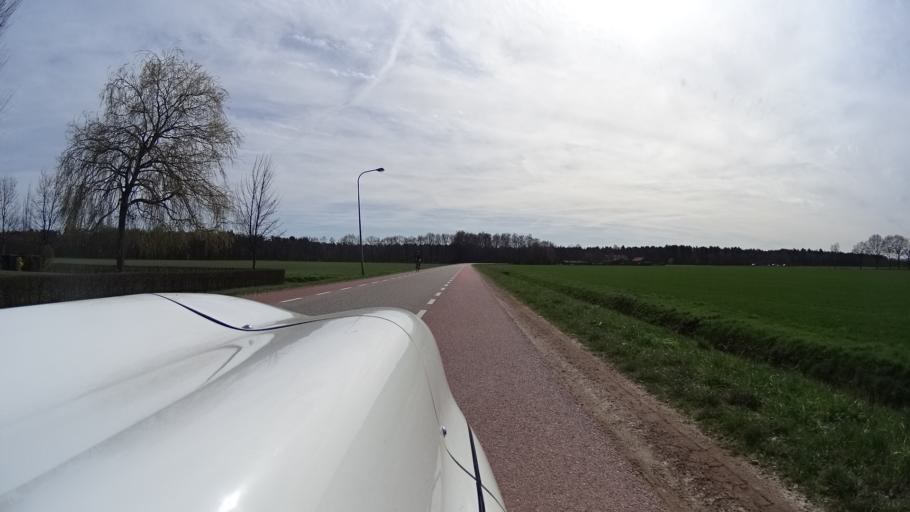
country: NL
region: Limburg
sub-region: Gemeente Venlo
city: Arcen
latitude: 51.5152
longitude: 6.2043
